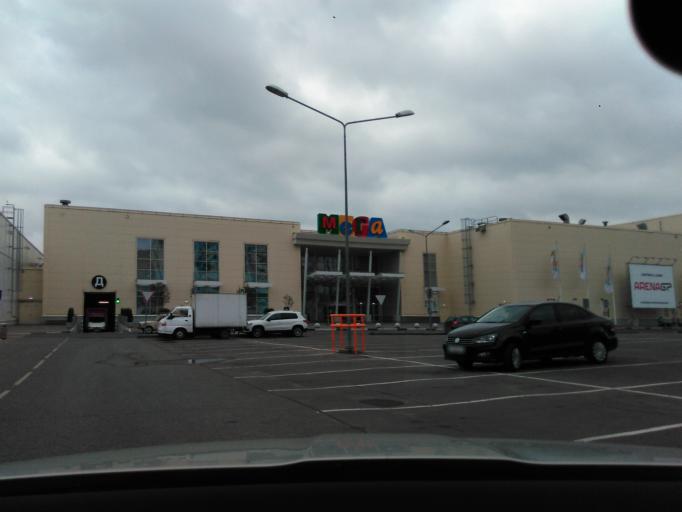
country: RU
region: Moscow
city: Khimki
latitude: 55.9113
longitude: 37.3925
